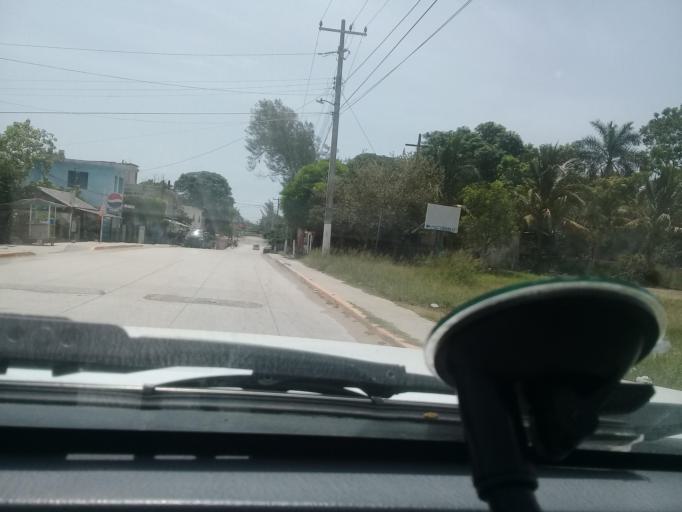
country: MX
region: Veracruz
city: Anahuac
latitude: 22.2291
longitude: -97.8296
